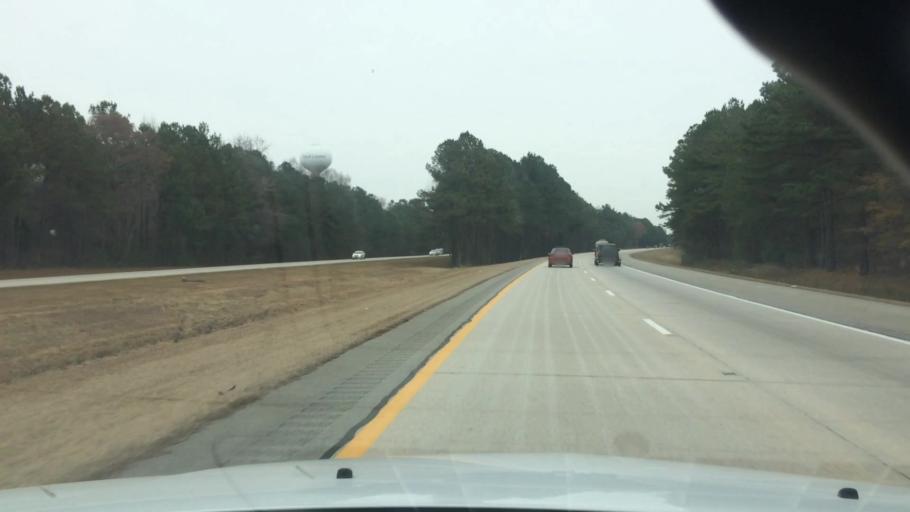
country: US
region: North Carolina
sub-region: Nash County
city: Nashville
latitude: 35.8804
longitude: -77.9479
